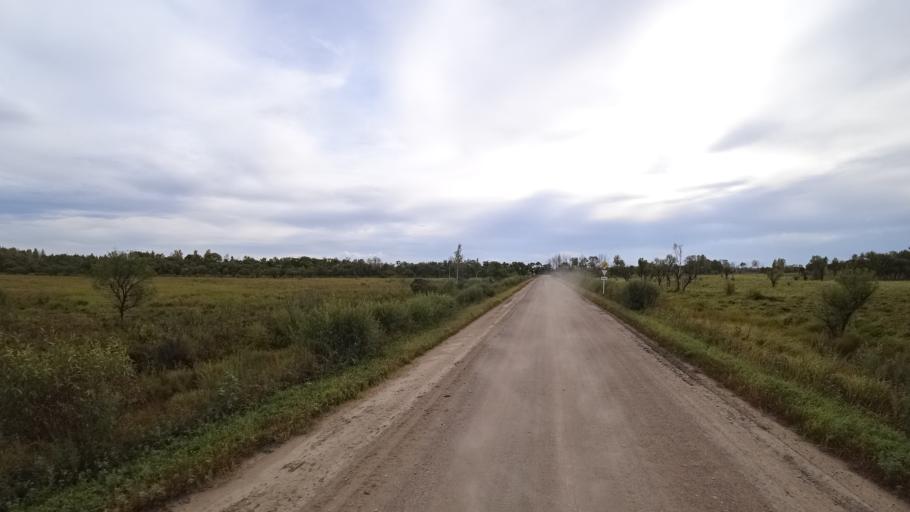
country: RU
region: Amur
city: Arkhara
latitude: 49.3752
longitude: 130.2078
